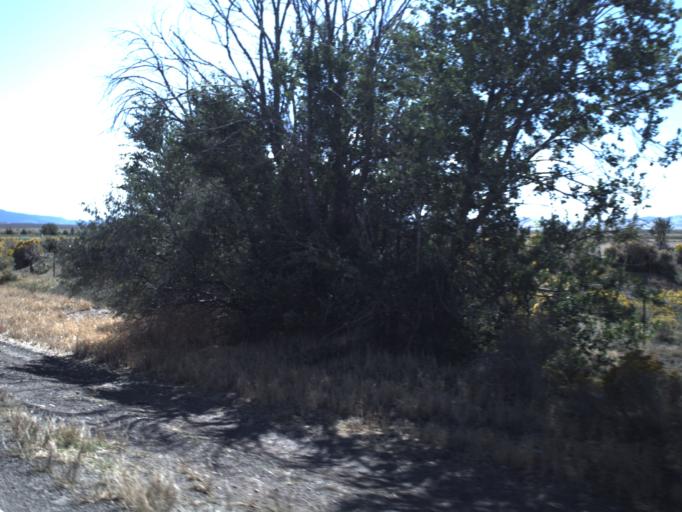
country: US
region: Utah
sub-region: Beaver County
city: Milford
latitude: 38.3384
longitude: -112.9762
